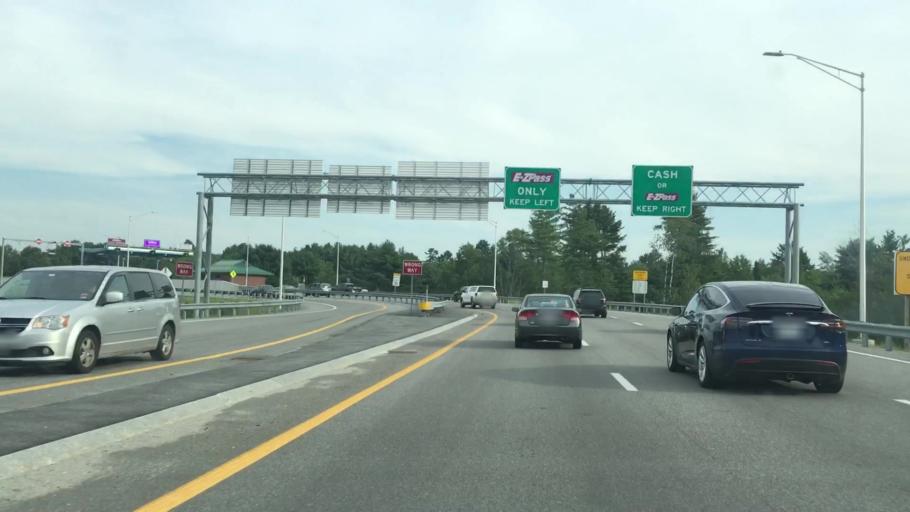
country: US
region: Maine
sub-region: Cumberland County
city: New Gloucester
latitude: 43.8825
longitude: -70.3388
